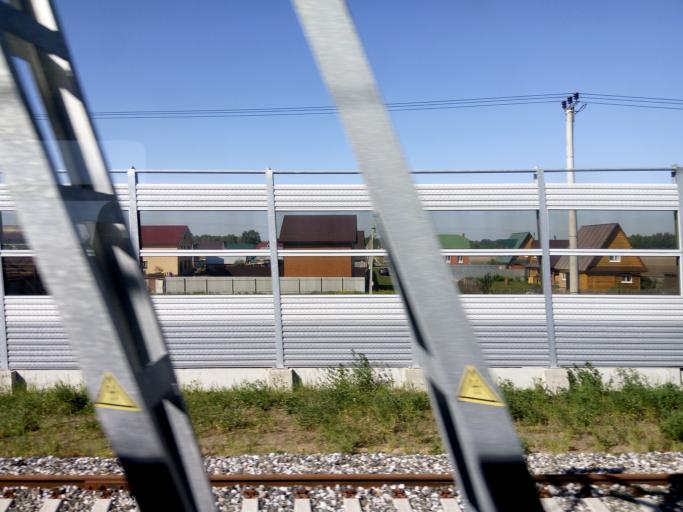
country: RU
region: Tatarstan
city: Stolbishchi
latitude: 55.6714
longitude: 49.2133
